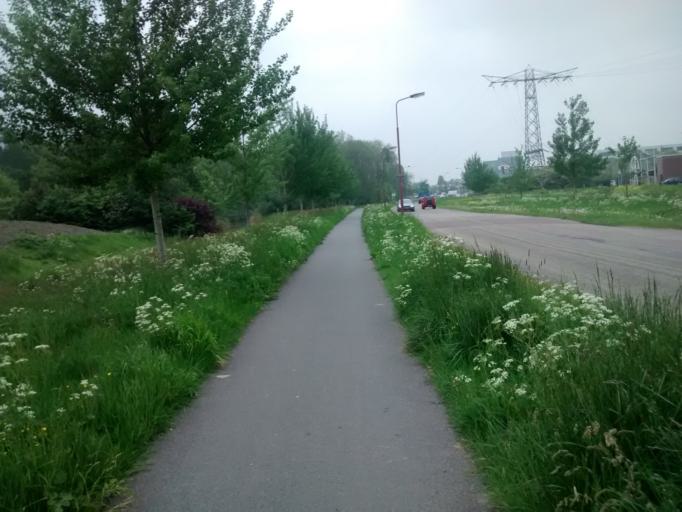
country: NL
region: Utrecht
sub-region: Gemeente Utrecht
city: Lunetten
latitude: 52.0497
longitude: 5.1240
